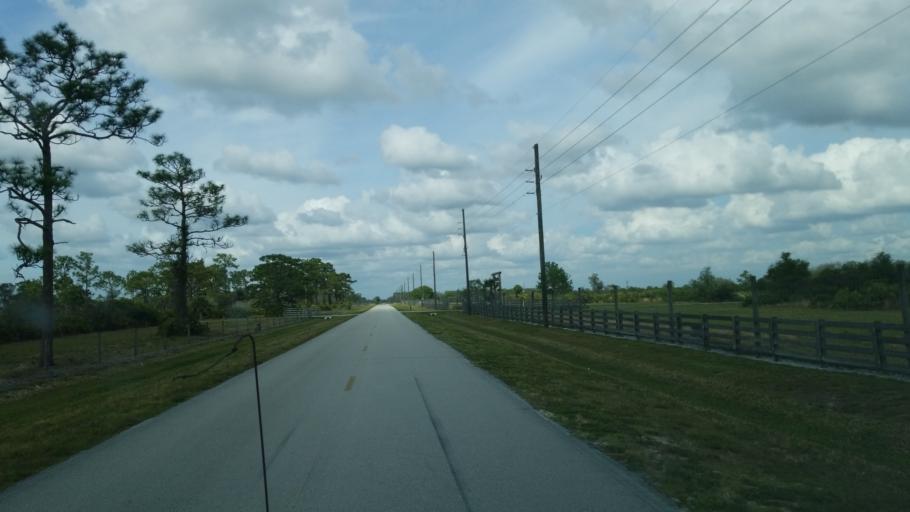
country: US
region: Florida
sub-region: Okeechobee County
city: Cypress Quarters
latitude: 27.4966
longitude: -80.7744
